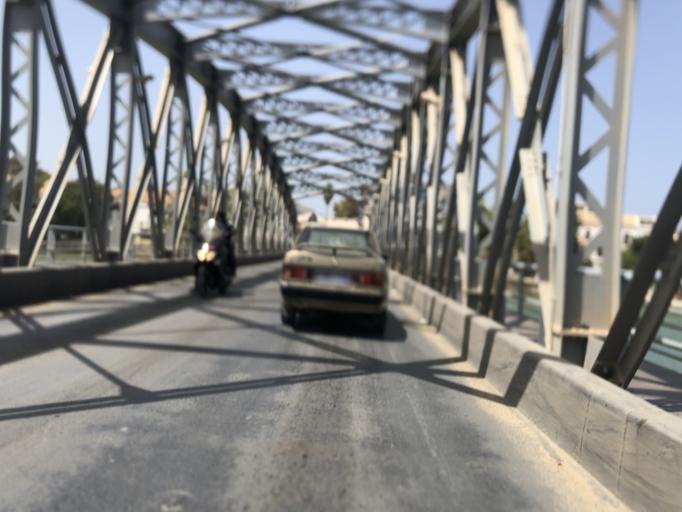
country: SN
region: Saint-Louis
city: Saint-Louis
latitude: 16.0253
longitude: -16.5002
